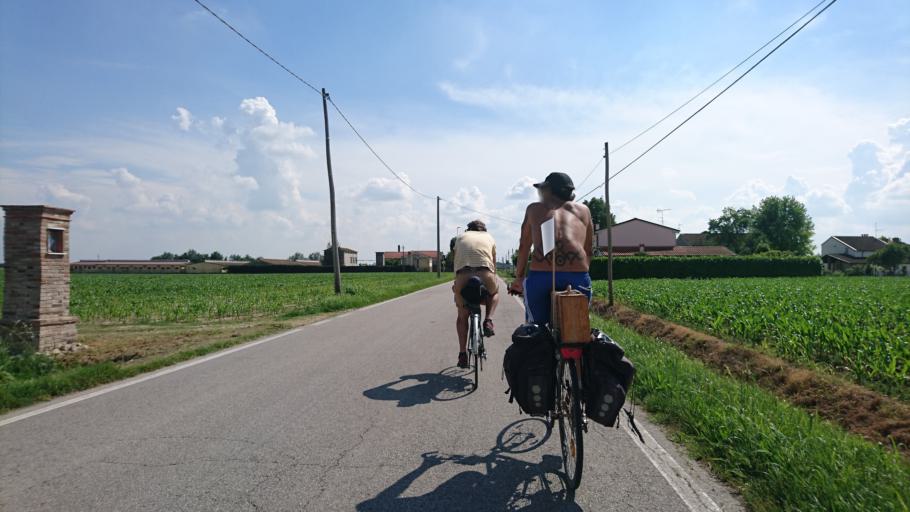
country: IT
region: Veneto
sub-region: Provincia di Rovigo
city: Castelmassa
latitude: 45.0533
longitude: 11.3266
